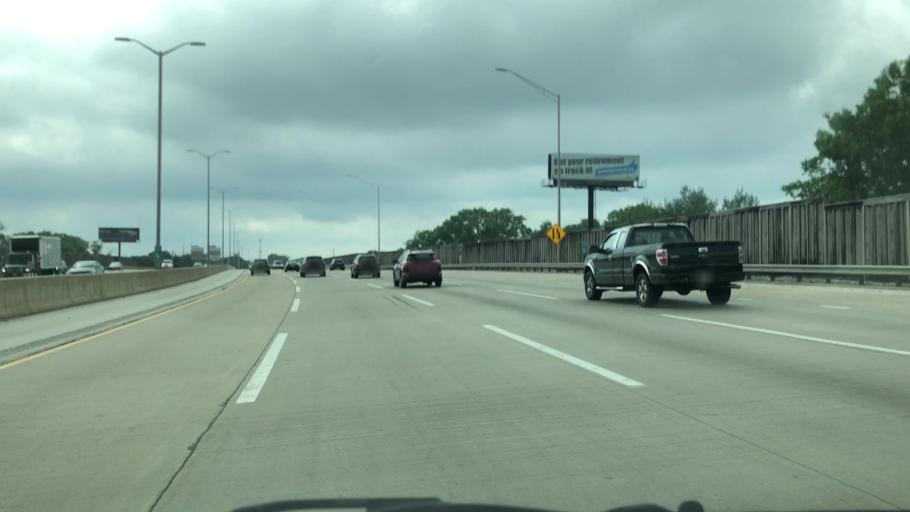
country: US
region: Illinois
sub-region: Cook County
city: Robbins
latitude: 41.6332
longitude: -87.7016
